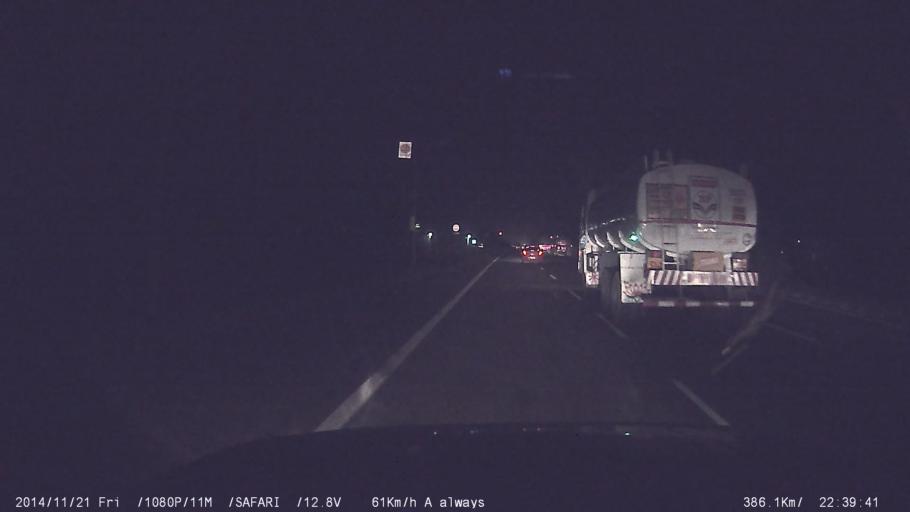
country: IN
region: Tamil Nadu
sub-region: Villupuram
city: Tindivanam
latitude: 12.2668
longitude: 79.6844
